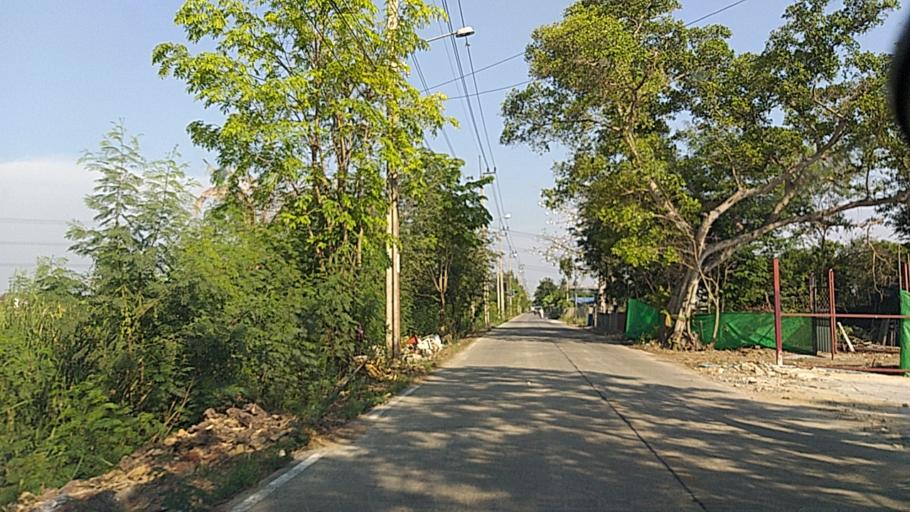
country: TH
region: Nonthaburi
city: Sai Noi
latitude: 13.9381
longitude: 100.3379
